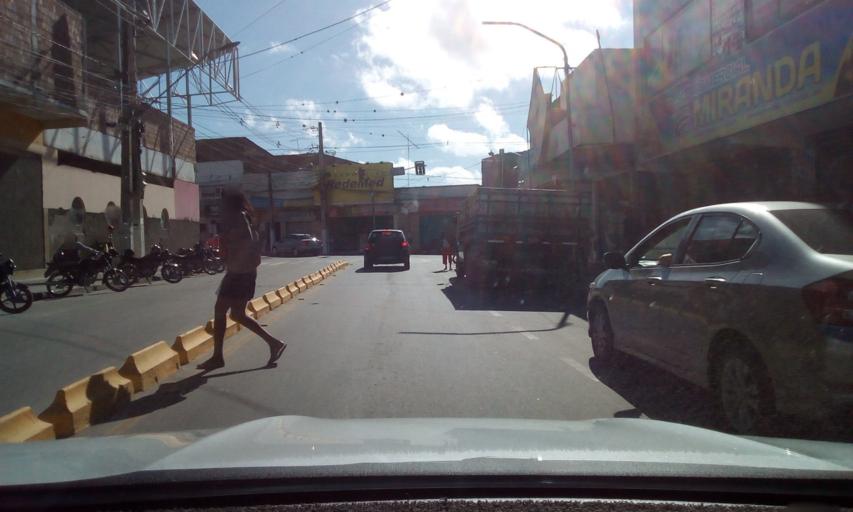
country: BR
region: Paraiba
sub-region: Fagundes
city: Fagundes
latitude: -7.3635
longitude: -35.9017
